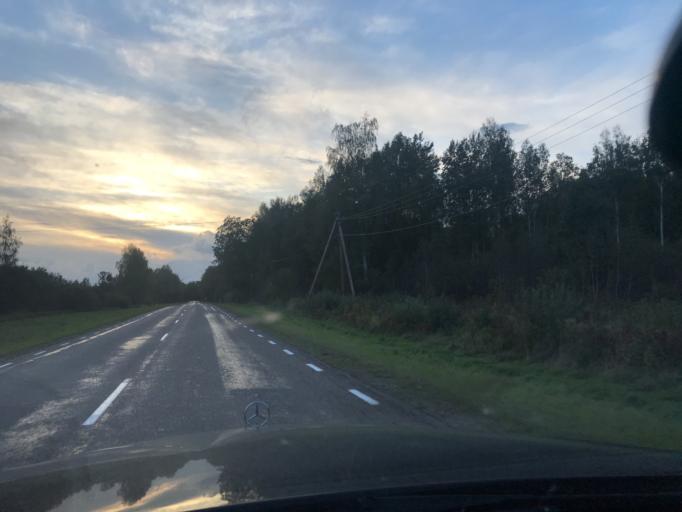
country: EE
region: Valgamaa
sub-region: Torva linn
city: Torva
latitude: 58.0086
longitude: 26.2189
